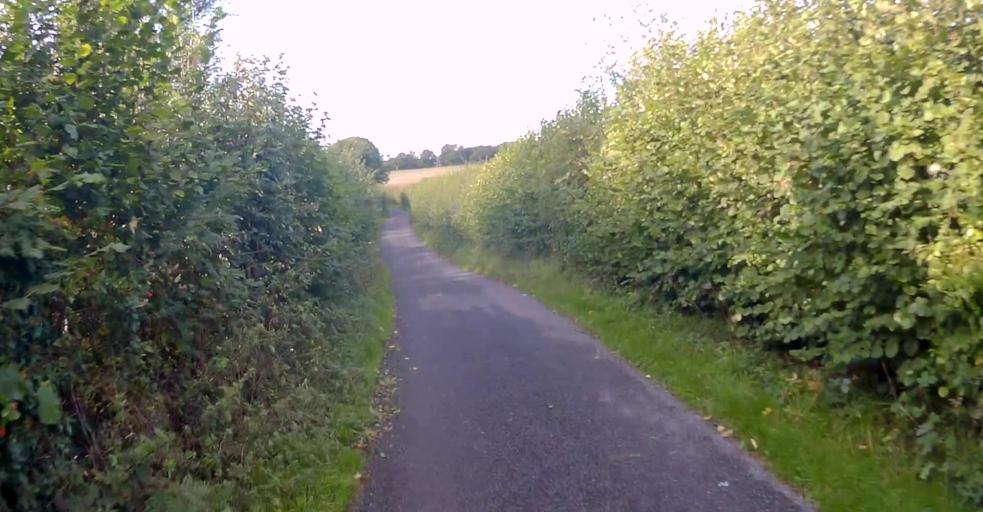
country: GB
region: England
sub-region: Surrey
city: Farnham
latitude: 51.2082
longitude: -0.8494
